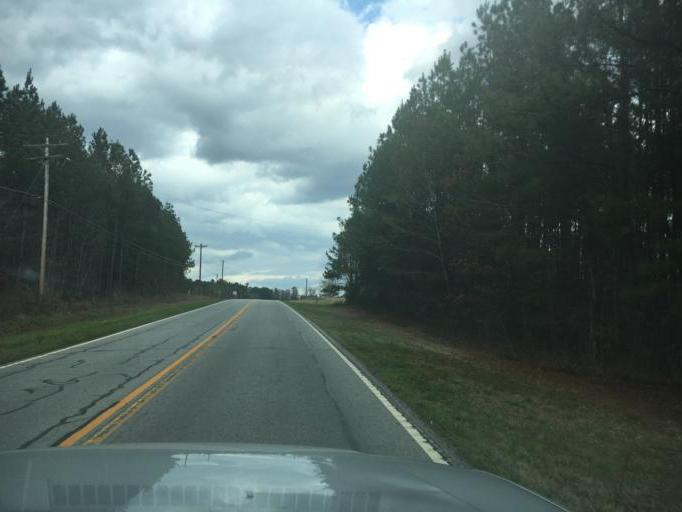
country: US
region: South Carolina
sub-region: Oconee County
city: Westminster
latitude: 34.6894
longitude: -83.0818
